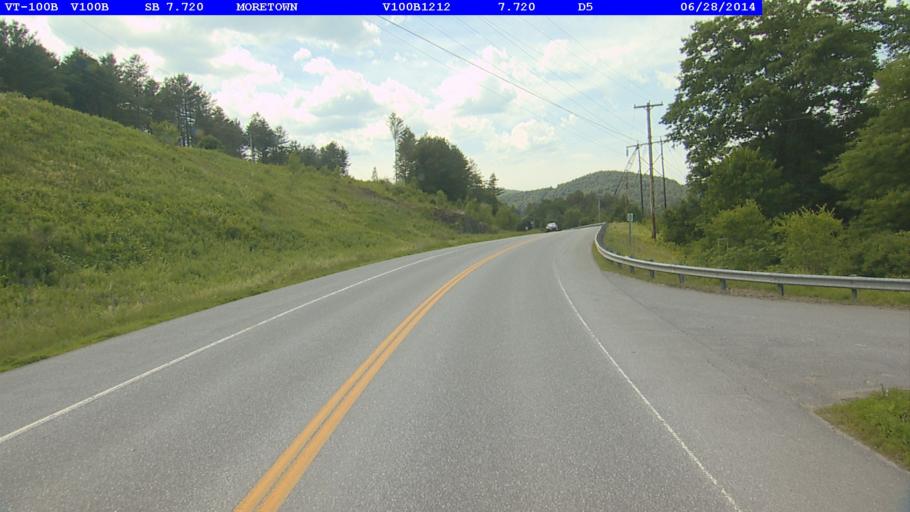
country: US
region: Vermont
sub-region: Washington County
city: Waterbury
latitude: 44.2910
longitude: -72.6812
